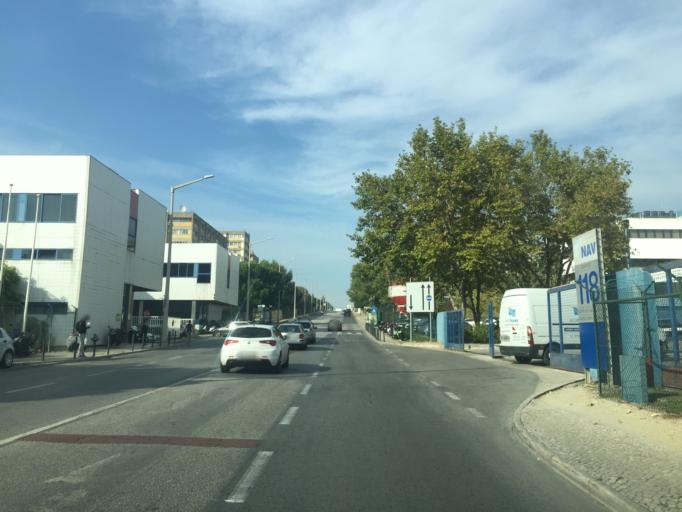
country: PT
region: Lisbon
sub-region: Loures
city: Moscavide
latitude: 38.7737
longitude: -9.1258
